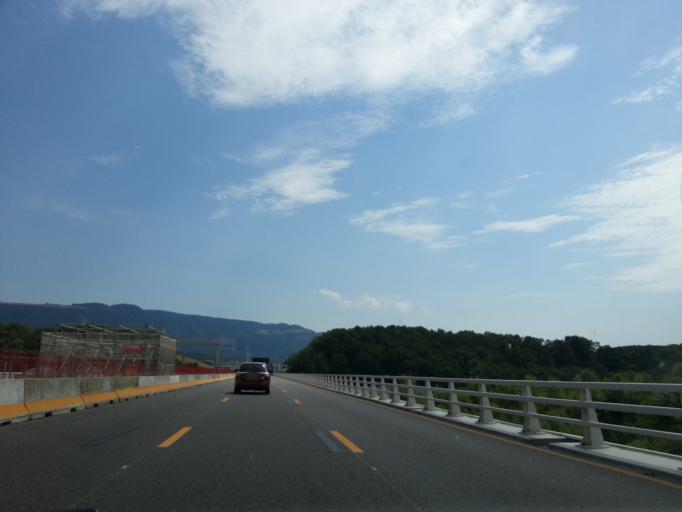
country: FR
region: Rhone-Alpes
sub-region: Departement de la Haute-Savoie
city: Saint-Julien-en-Genevois
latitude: 46.1449
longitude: 6.0964
